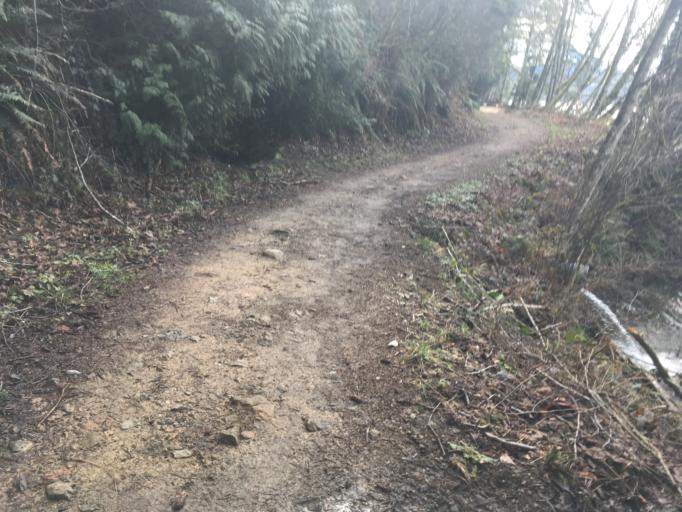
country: US
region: Washington
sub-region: Whatcom County
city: Sudden Valley
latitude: 48.6986
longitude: -122.2975
